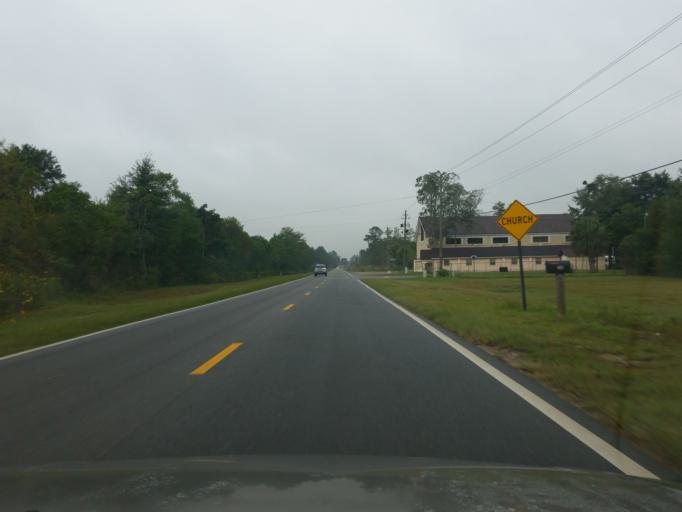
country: US
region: Florida
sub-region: Escambia County
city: Cantonment
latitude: 30.6072
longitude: -87.3351
